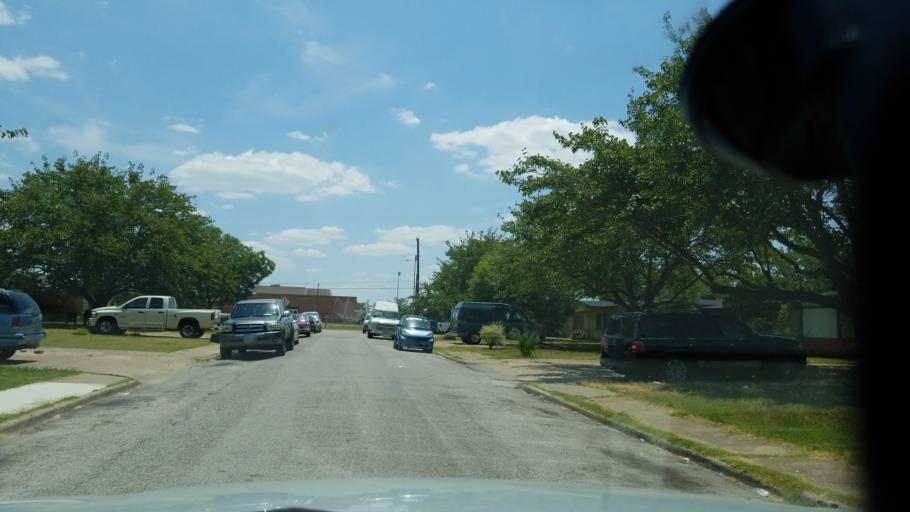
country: US
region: Texas
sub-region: Dallas County
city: Grand Prairie
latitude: 32.7539
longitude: -96.9648
